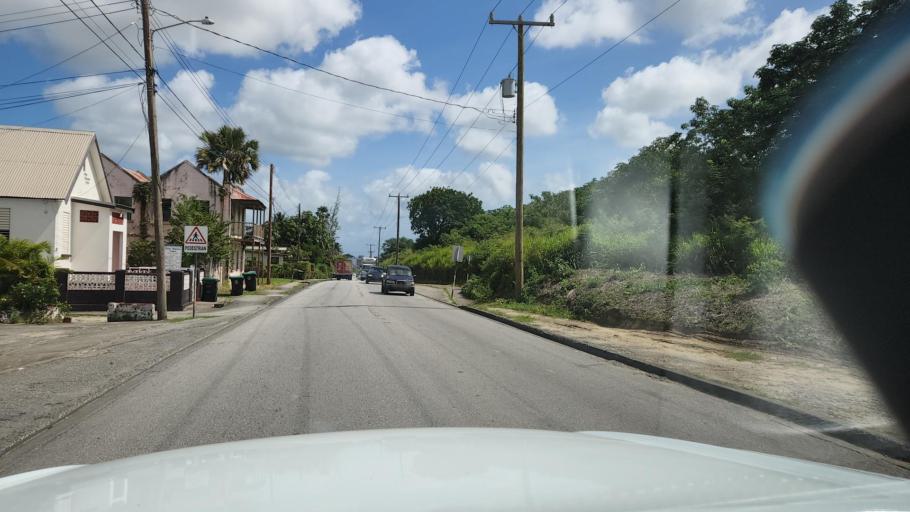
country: BB
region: Christ Church
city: Oistins
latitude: 13.1091
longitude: -59.5481
